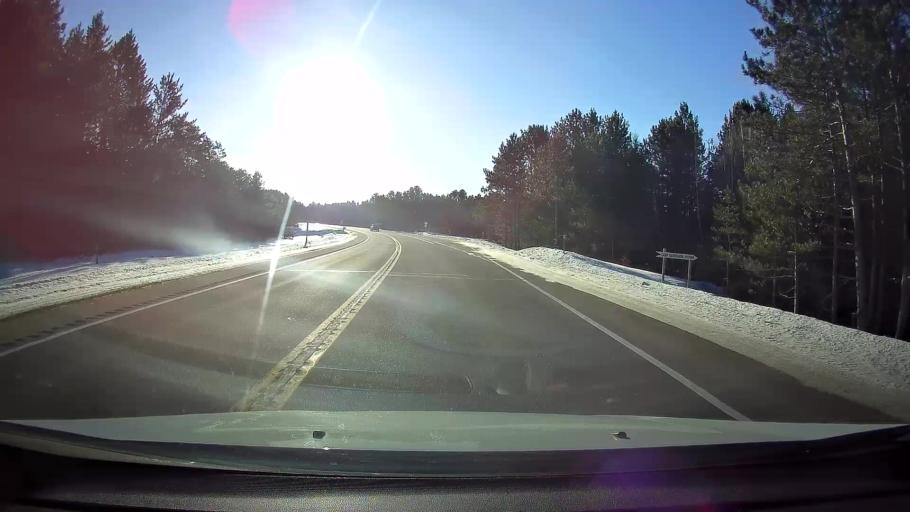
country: US
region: Wisconsin
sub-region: Sawyer County
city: Hayward
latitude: 45.9891
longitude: -91.5921
